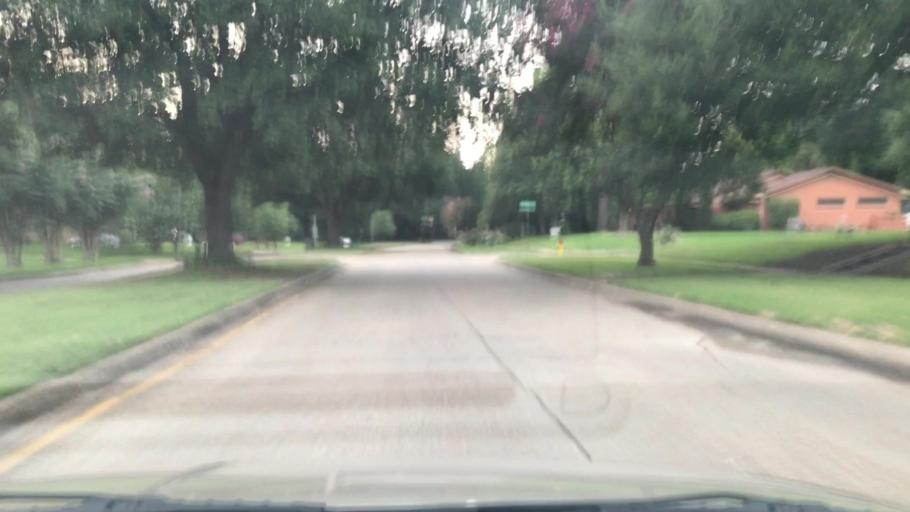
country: US
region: Louisiana
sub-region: Bossier Parish
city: Bossier City
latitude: 32.4534
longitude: -93.7324
